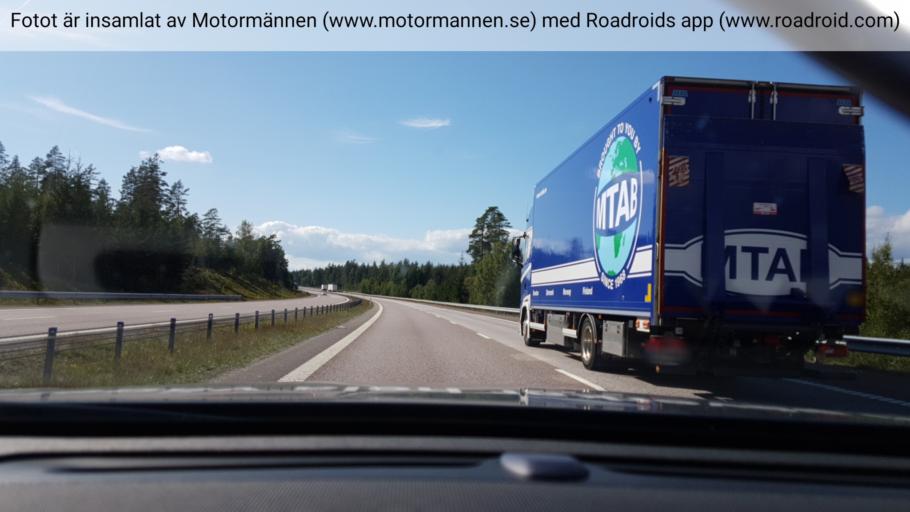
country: SE
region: OEstergoetland
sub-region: Norrkopings Kommun
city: Krokek
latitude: 58.7486
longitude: 16.4552
